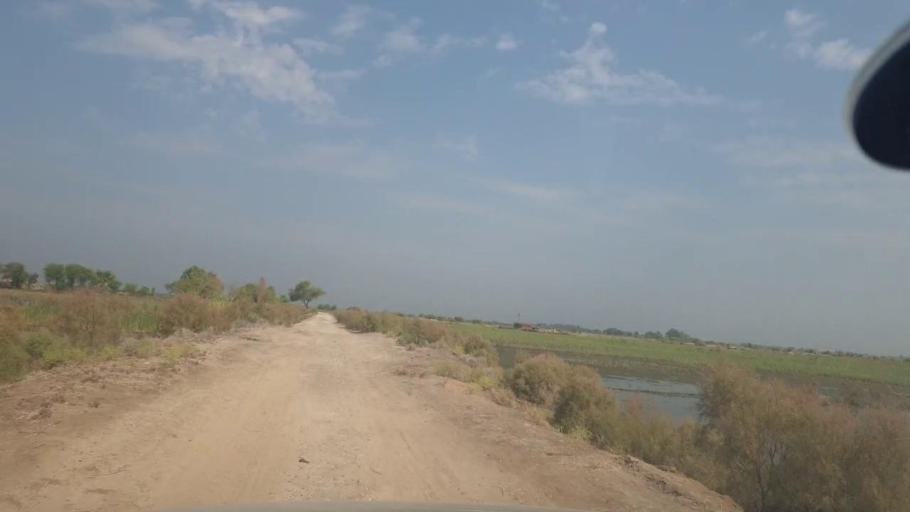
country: PK
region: Balochistan
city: Mehrabpur
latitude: 28.0339
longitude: 68.1289
